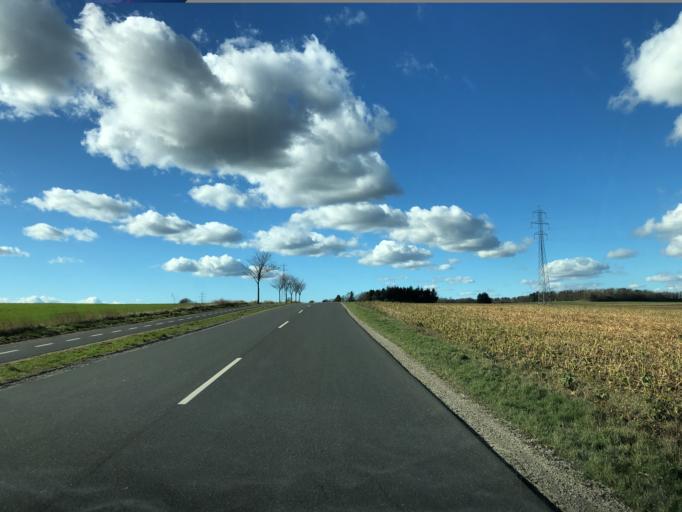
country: DK
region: Central Jutland
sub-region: Favrskov Kommune
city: Hinnerup
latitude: 56.2803
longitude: 10.0343
